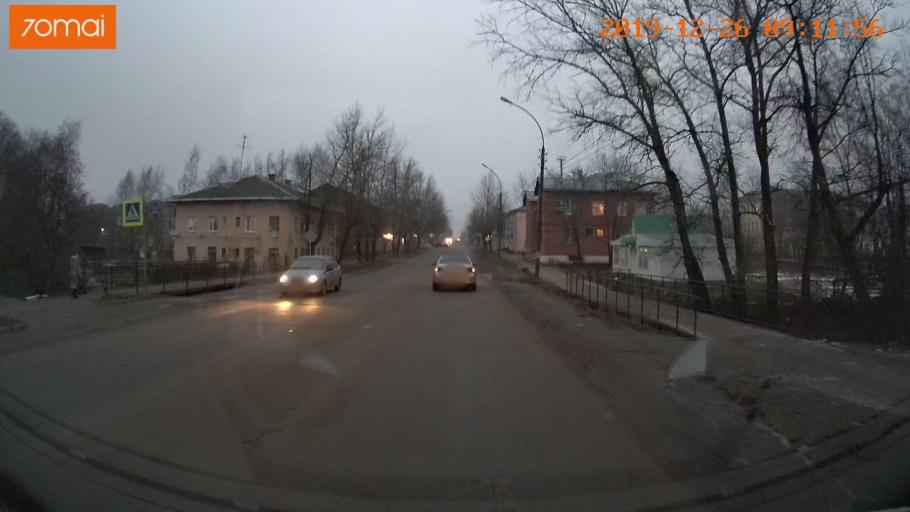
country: RU
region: Vologda
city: Gryazovets
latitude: 58.8784
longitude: 40.2530
